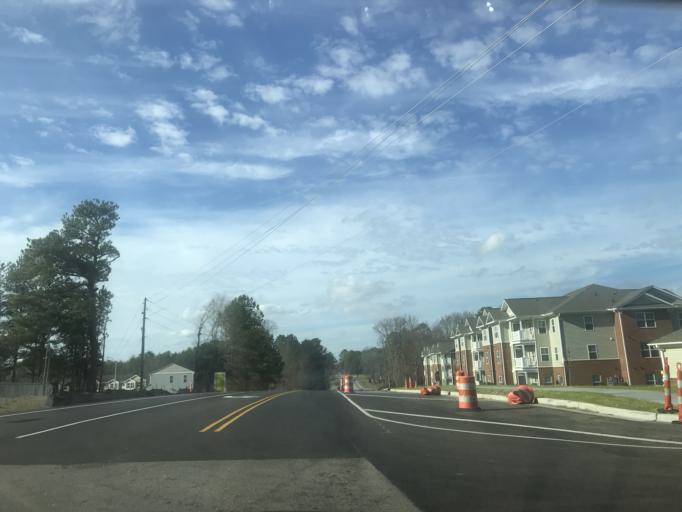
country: US
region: North Carolina
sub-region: Wake County
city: Garner
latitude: 35.7281
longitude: -78.5532
